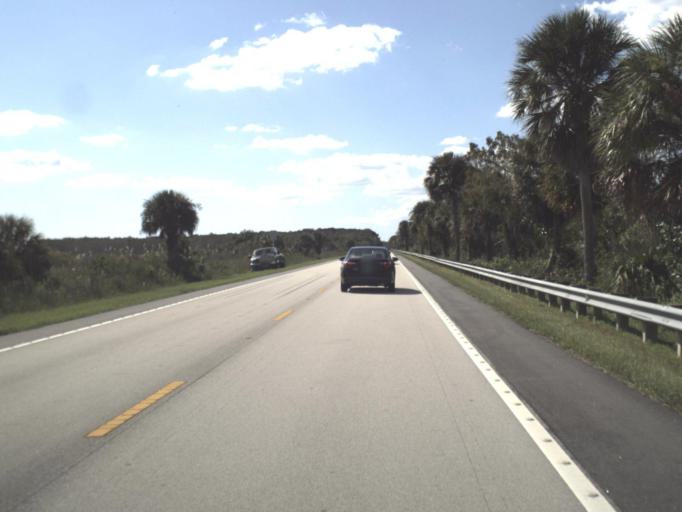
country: US
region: Florida
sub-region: Collier County
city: Marco
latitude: 25.8756
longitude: -81.2169
